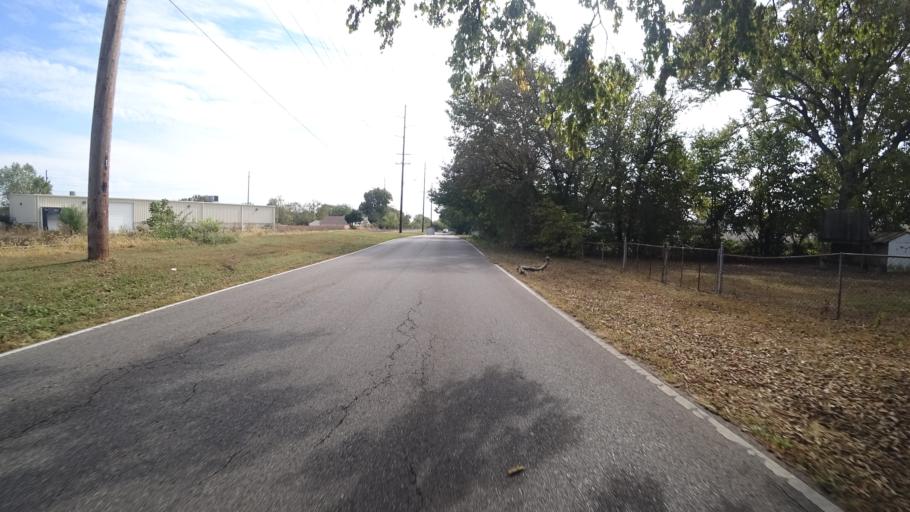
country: US
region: Ohio
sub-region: Butler County
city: Fairfield
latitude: 39.3606
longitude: -84.5440
